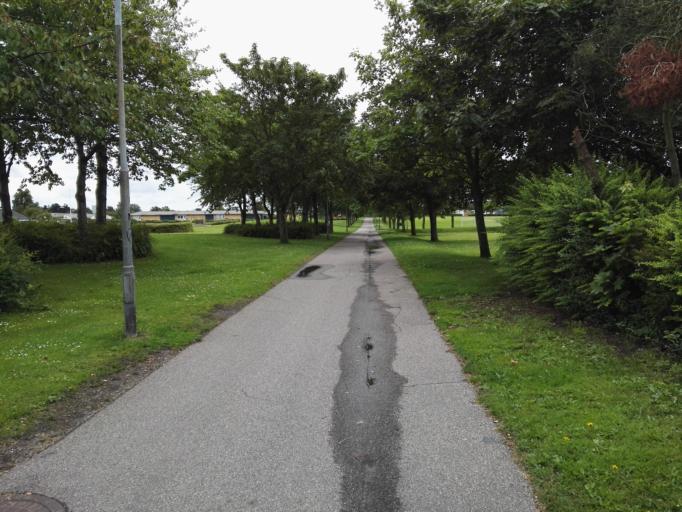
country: DK
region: Capital Region
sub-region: Egedal Kommune
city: Olstykke
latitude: 55.7775
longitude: 12.1680
